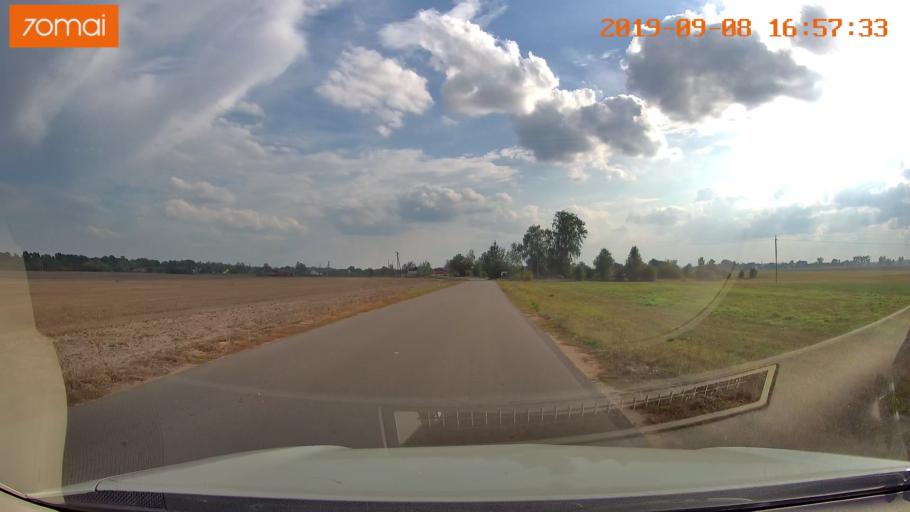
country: BY
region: Grodnenskaya
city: Hrodna
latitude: 53.7316
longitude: 23.9277
